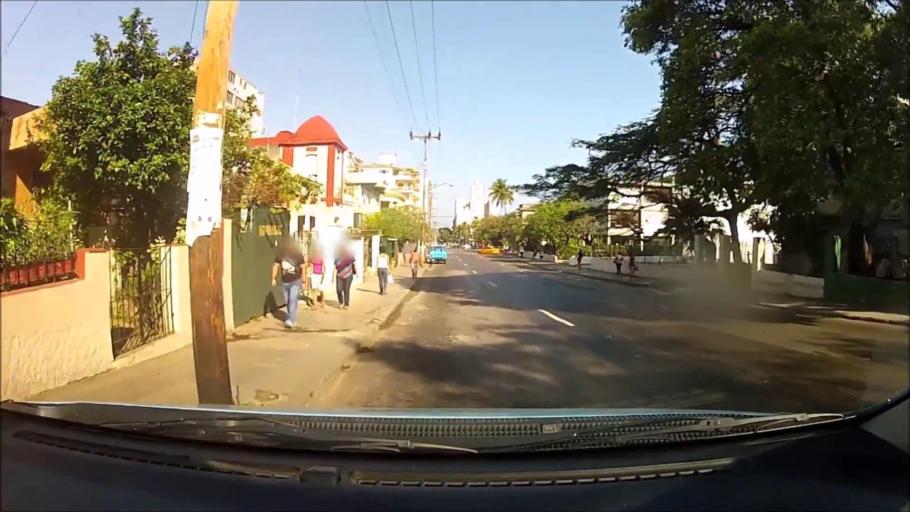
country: CU
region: La Habana
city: Havana
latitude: 23.1410
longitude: -82.3846
